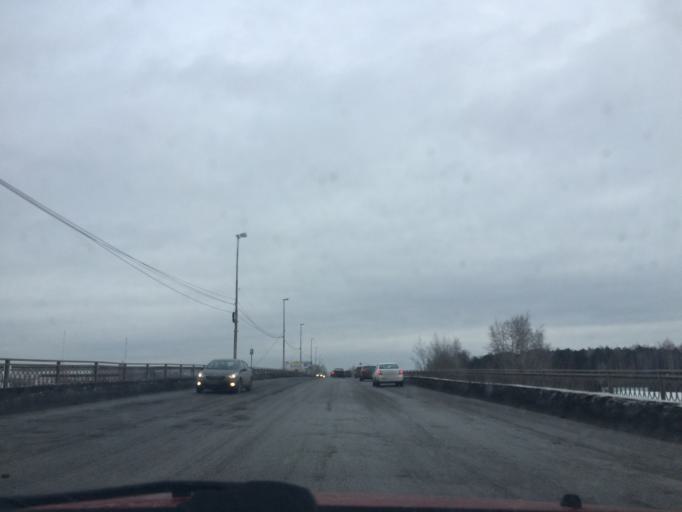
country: RU
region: Sverdlovsk
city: Yekaterinburg
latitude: 56.8658
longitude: 60.6714
